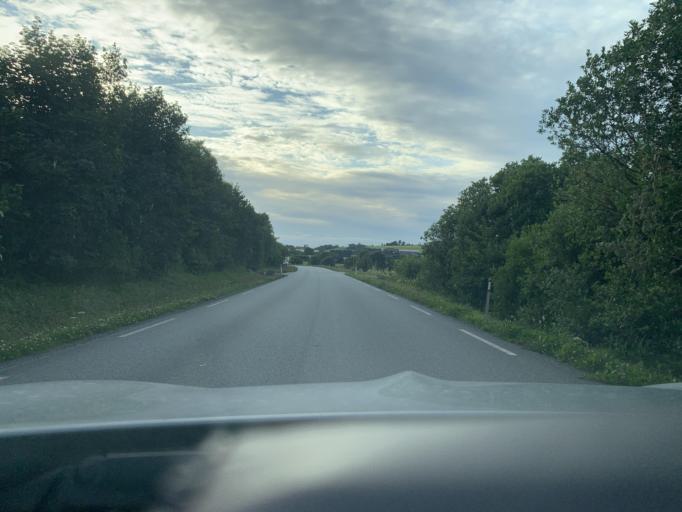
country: NO
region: Rogaland
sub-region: Time
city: Bryne
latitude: 58.6986
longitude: 5.7096
